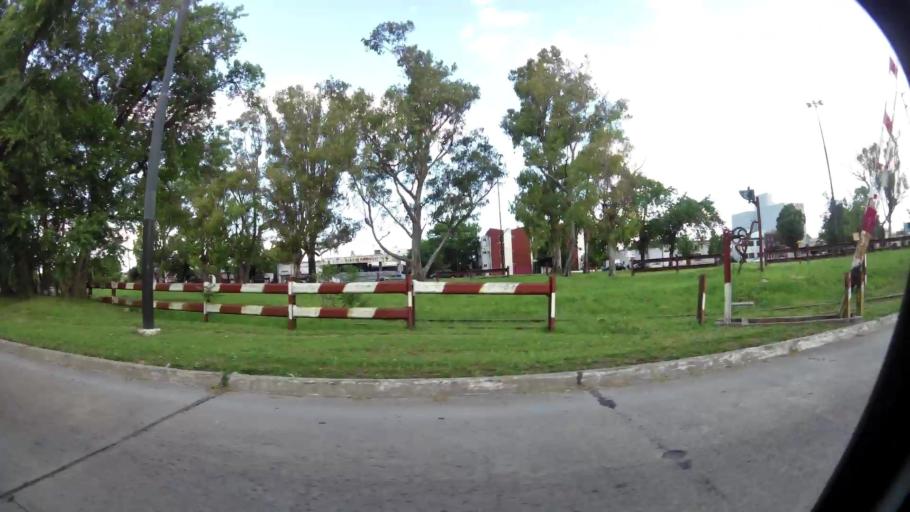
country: AR
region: Buenos Aires
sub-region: Partido de La Plata
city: La Plata
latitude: -34.8936
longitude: -57.9622
